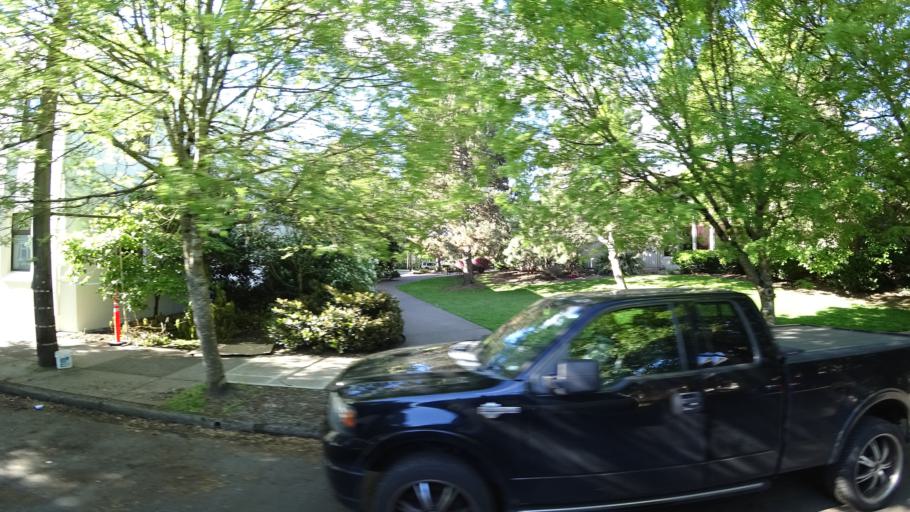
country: US
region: Oregon
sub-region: Multnomah County
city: Portland
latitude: 45.5215
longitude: -122.6515
